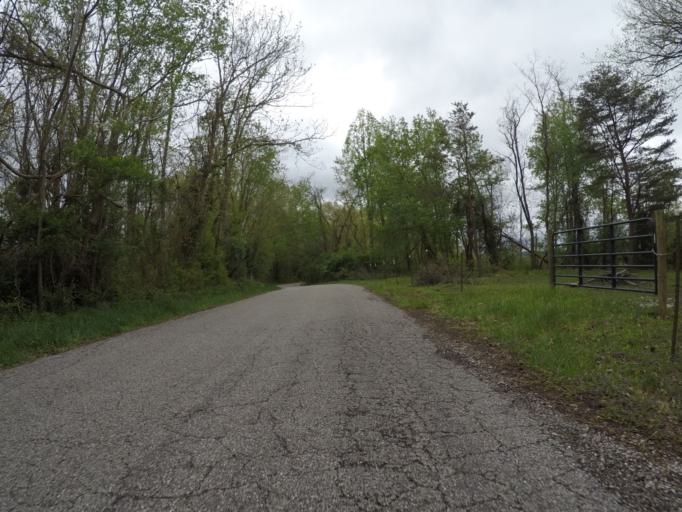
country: US
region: West Virginia
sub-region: Cabell County
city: Barboursville
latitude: 38.3939
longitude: -82.2512
